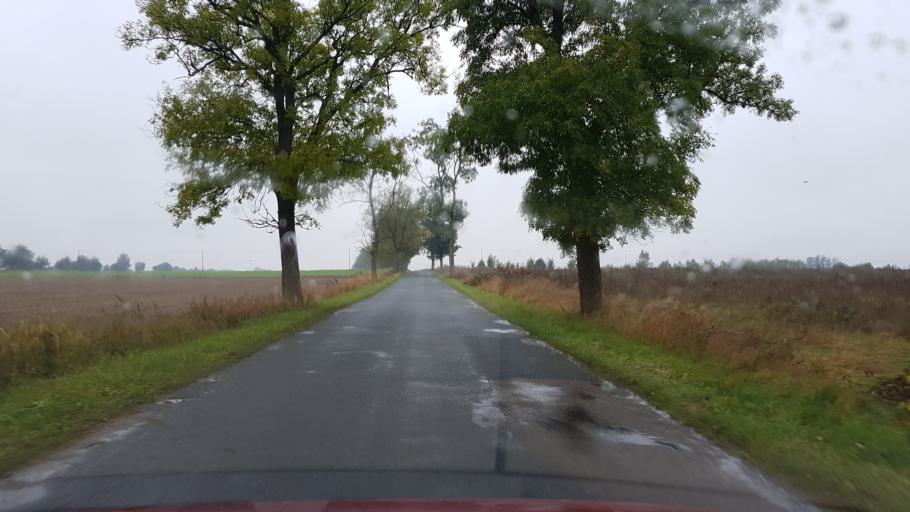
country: PL
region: Greater Poland Voivodeship
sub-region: Powiat zlotowski
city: Tarnowka
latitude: 53.3451
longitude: 16.8858
